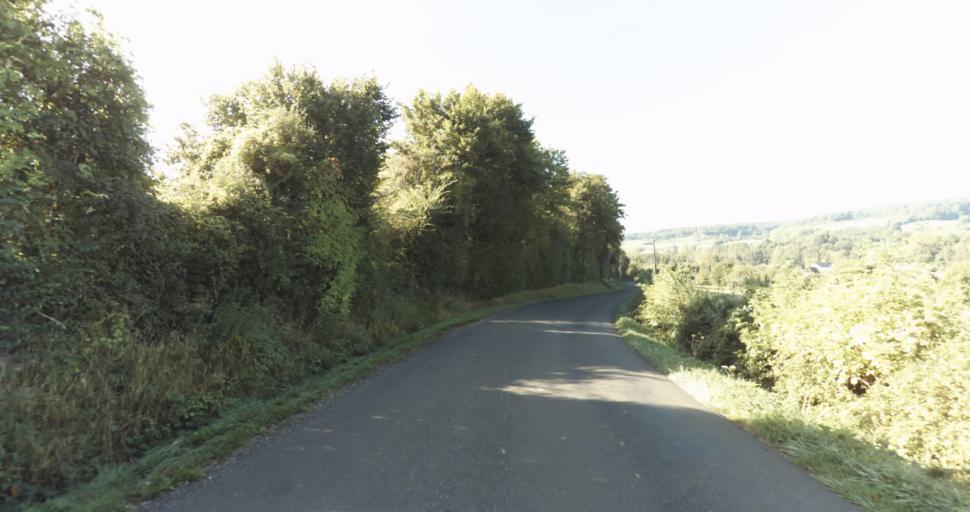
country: FR
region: Lower Normandy
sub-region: Departement de l'Orne
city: Vimoutiers
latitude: 48.9317
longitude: 0.2746
